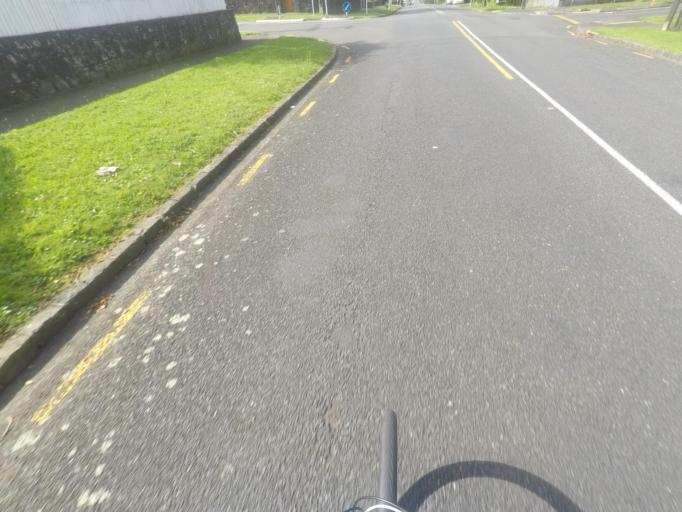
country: NZ
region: Auckland
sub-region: Auckland
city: Mangere
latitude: -36.9184
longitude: 174.7826
